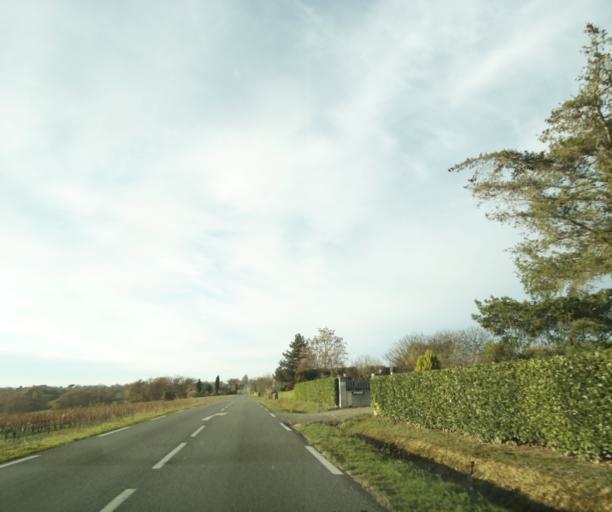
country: FR
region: Midi-Pyrenees
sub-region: Departement du Gers
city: Cazaubon
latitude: 43.9300
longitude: -0.0482
